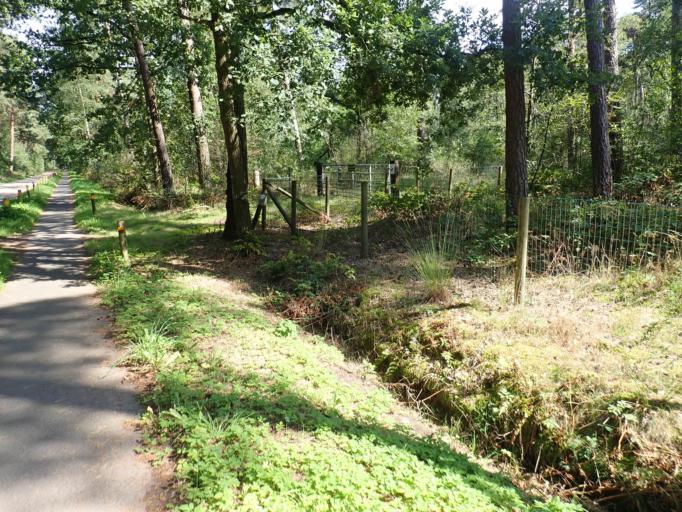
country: BE
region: Flanders
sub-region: Provincie Antwerpen
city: Oostmalle
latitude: 51.2862
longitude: 4.7590
